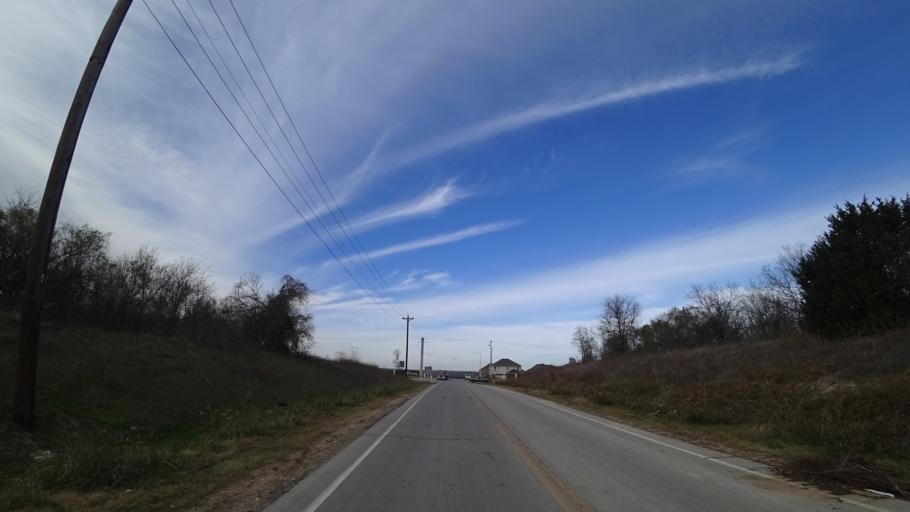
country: US
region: Texas
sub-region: Travis County
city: Onion Creek
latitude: 30.1585
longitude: -97.7278
